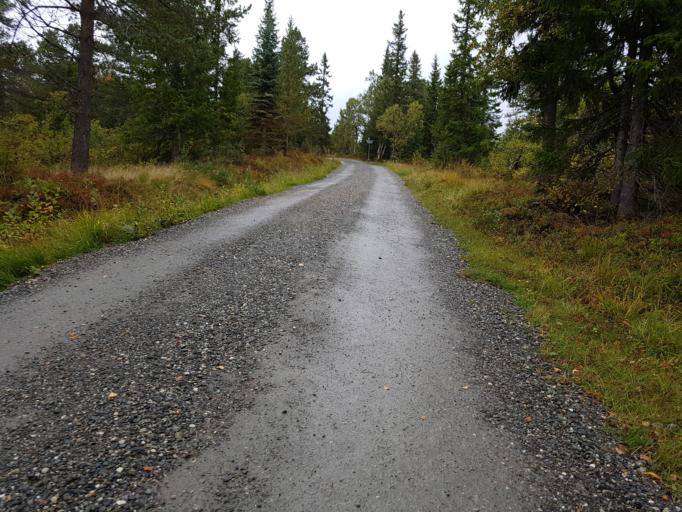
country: NO
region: Sor-Trondelag
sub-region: Melhus
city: Melhus
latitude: 63.4146
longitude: 10.2457
